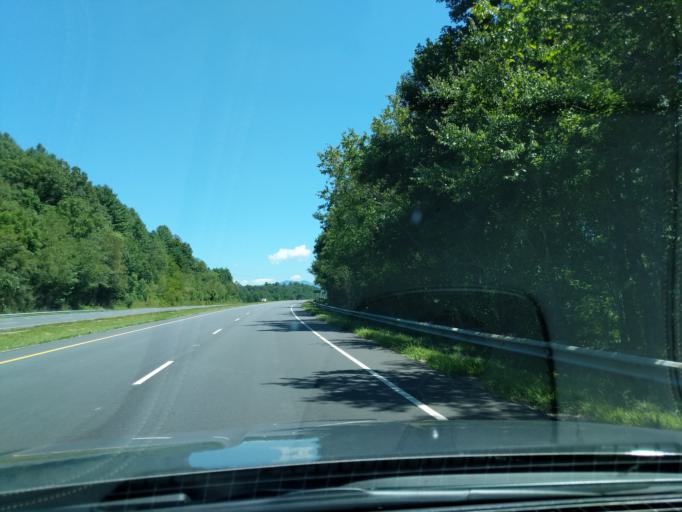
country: US
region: North Carolina
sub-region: Macon County
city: Franklin
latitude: 35.1565
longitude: -83.4605
